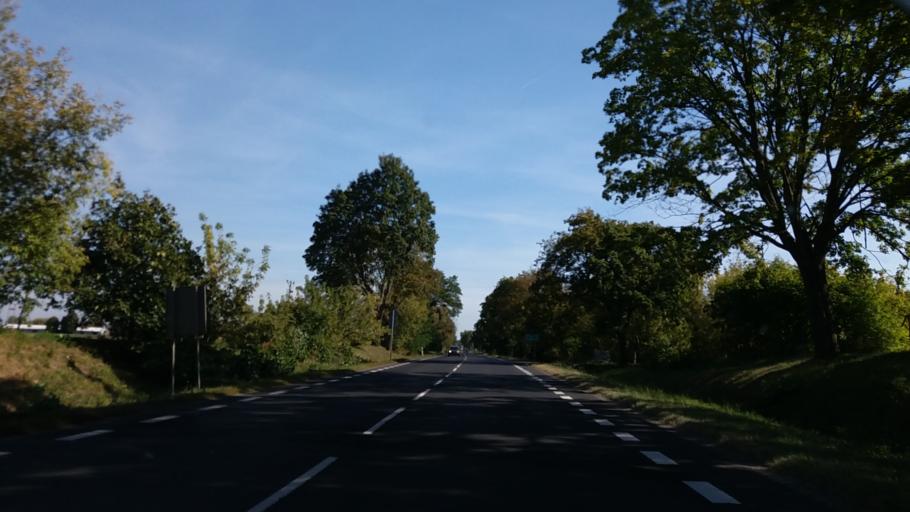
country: PL
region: Greater Poland Voivodeship
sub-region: Powiat miedzychodzki
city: Kwilcz
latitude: 52.5568
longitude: 16.0714
